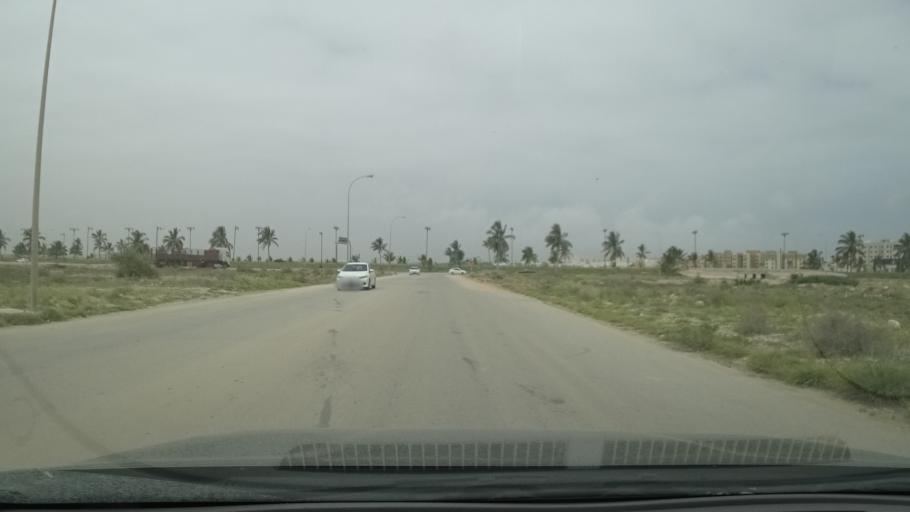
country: OM
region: Zufar
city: Salalah
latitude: 17.0260
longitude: 54.0567
